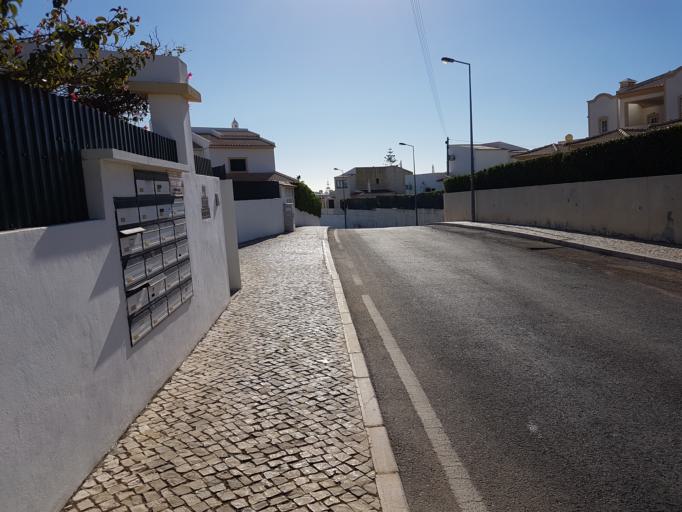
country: PT
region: Faro
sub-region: Albufeira
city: Albufeira
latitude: 37.0877
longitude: -8.2352
